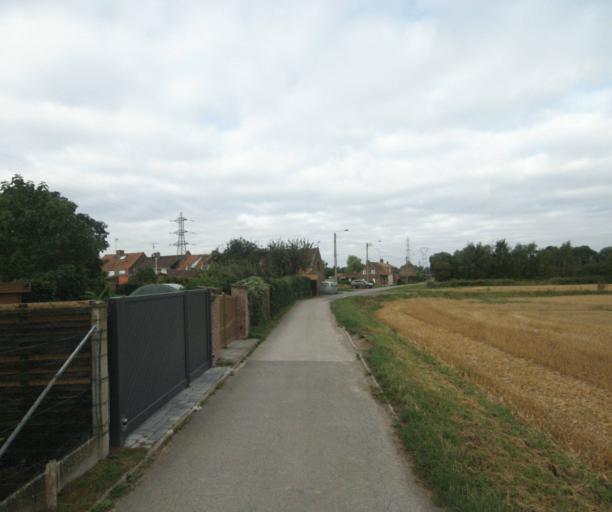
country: FR
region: Nord-Pas-de-Calais
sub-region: Departement du Nord
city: Hem
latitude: 50.6467
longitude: 3.1791
